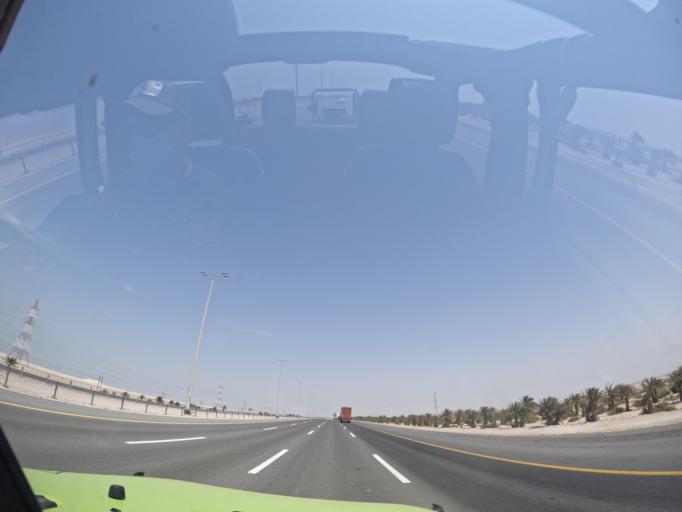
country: AE
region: Abu Dhabi
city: Abu Dhabi
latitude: 24.2022
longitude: 54.3998
